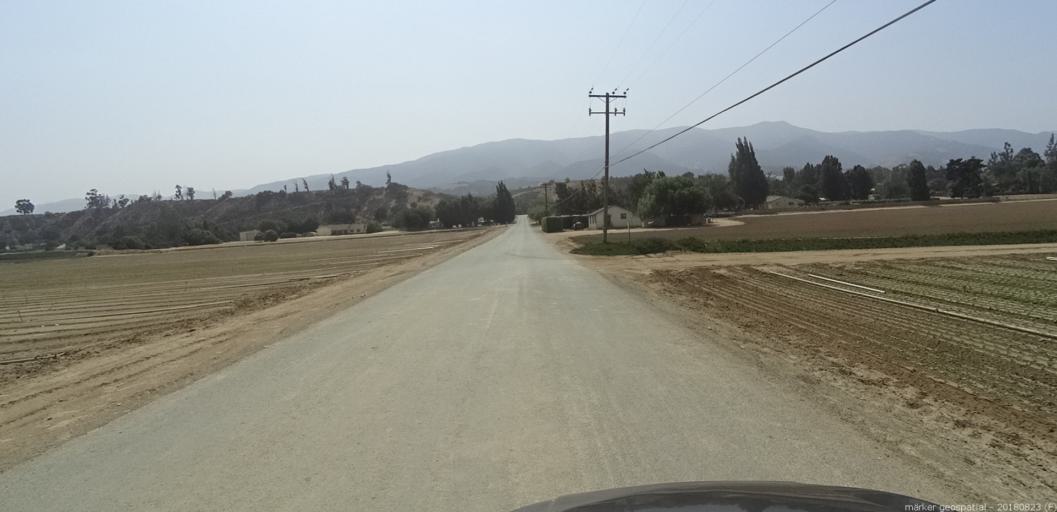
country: US
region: California
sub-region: Monterey County
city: Soledad
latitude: 36.3905
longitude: -121.3586
